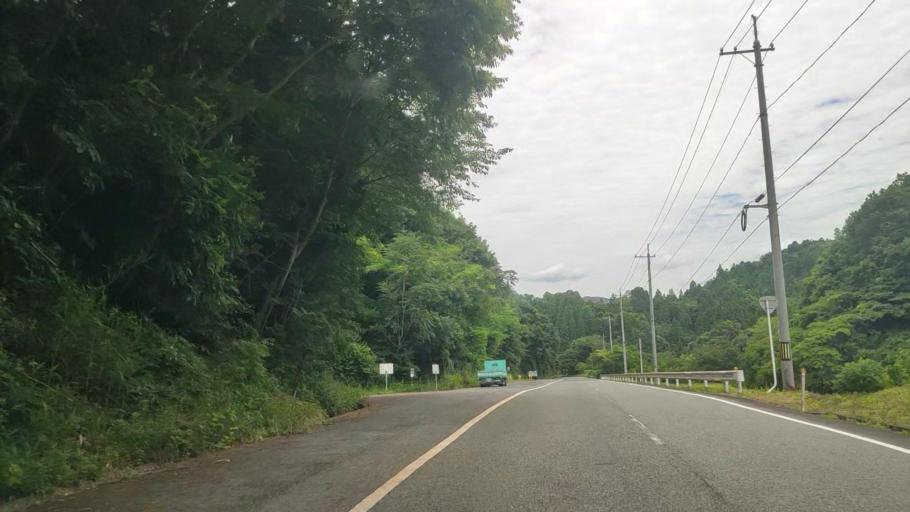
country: JP
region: Okayama
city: Tsuyama
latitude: 35.0947
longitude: 134.2675
